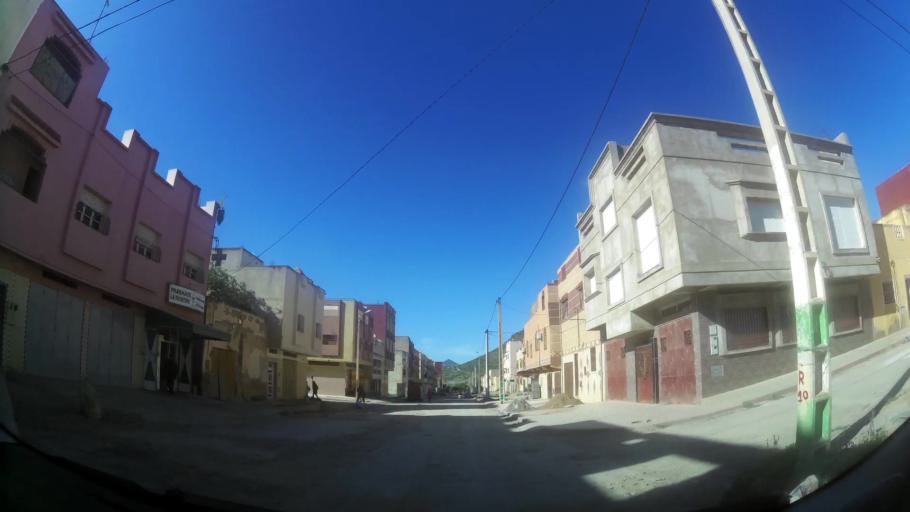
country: MA
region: Oriental
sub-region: Berkane-Taourirt
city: Ahfir
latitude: 34.9565
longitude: -2.0977
